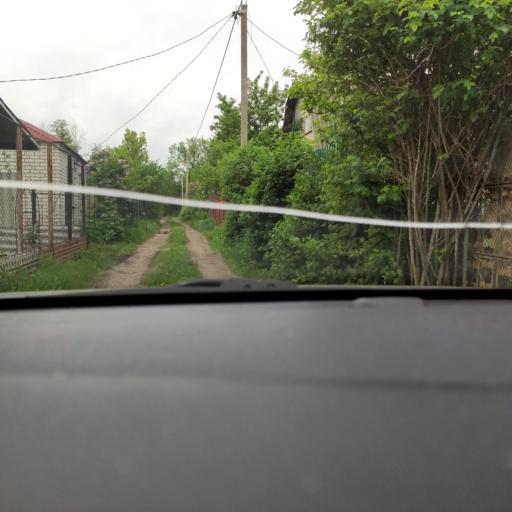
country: RU
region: Voronezj
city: Voronezh
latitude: 51.5948
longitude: 39.1663
